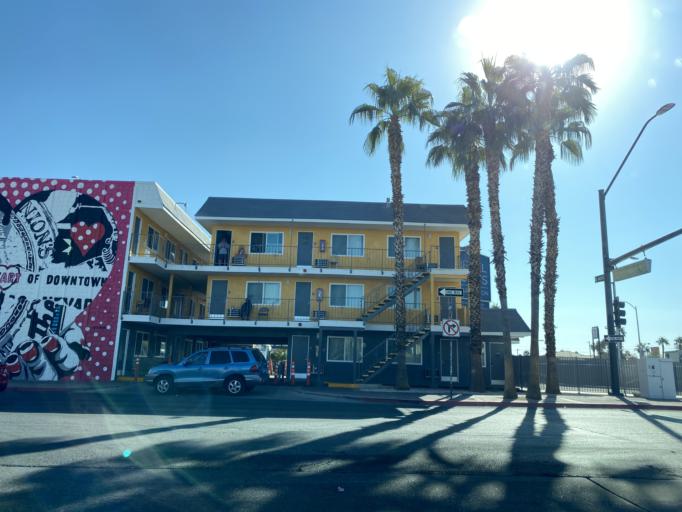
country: US
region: Nevada
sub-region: Clark County
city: Las Vegas
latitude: 36.1594
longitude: -115.1488
